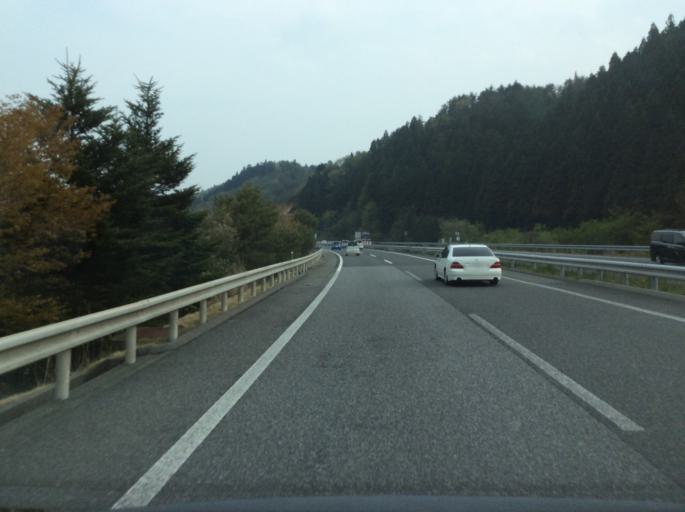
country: JP
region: Fukushima
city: Iwaki
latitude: 37.1149
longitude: 140.7521
